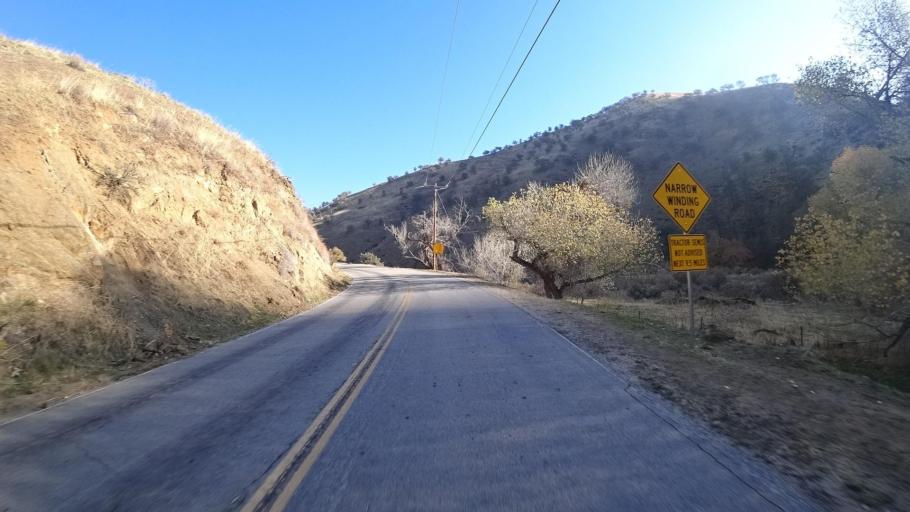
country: US
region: California
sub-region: Kern County
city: Bear Valley Springs
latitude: 35.3042
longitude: -118.5842
